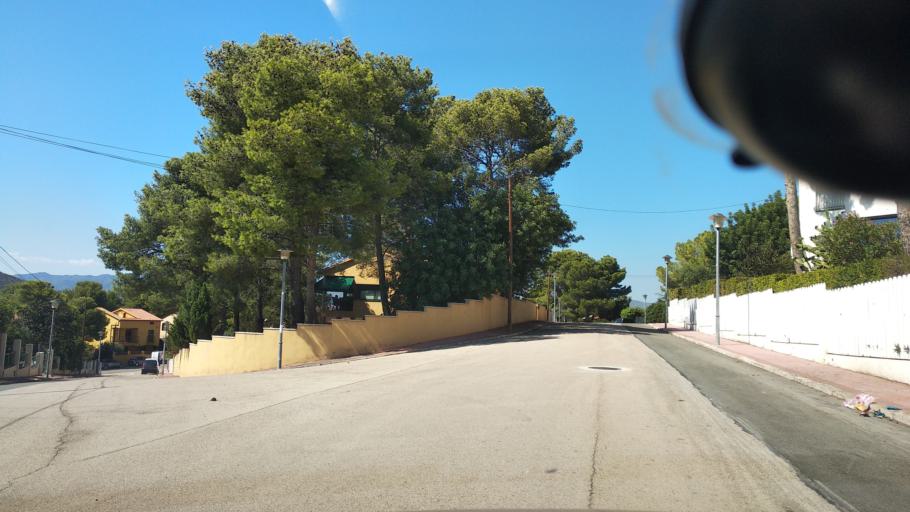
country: ES
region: Catalonia
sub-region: Provincia de Tarragona
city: El Vendrell
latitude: 41.2212
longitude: 1.5449
